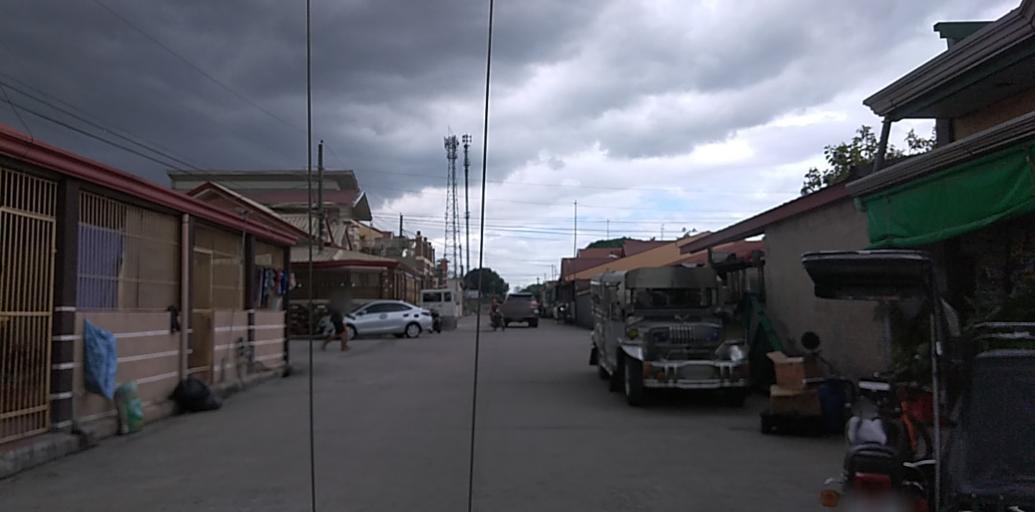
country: PH
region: Central Luzon
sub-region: Province of Pampanga
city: Pio
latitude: 15.0461
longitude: 120.5310
